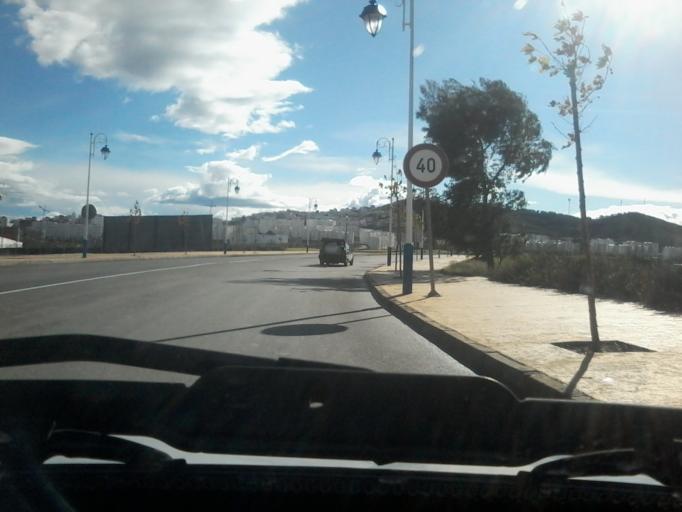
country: MA
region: Tanger-Tetouan
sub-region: Tetouan
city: Martil
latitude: 35.6940
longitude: -5.3423
